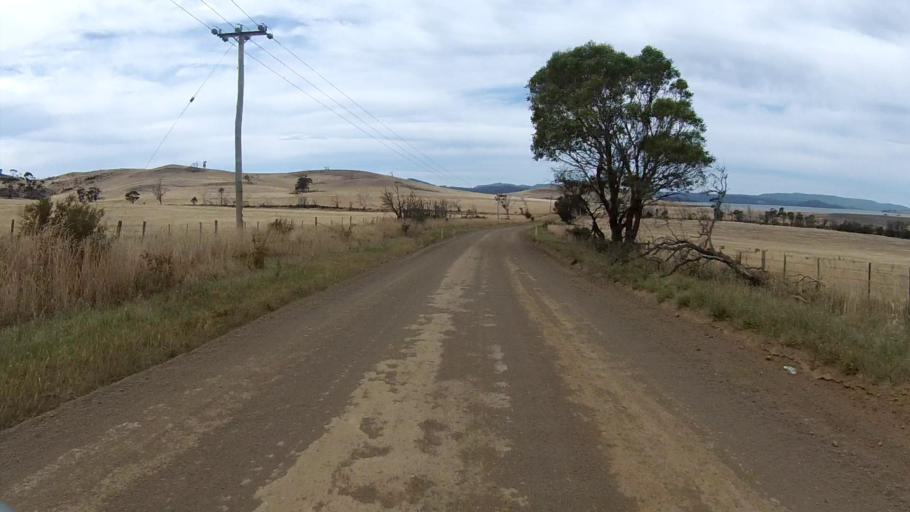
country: AU
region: Tasmania
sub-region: Sorell
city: Sorell
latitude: -42.8956
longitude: 147.7507
